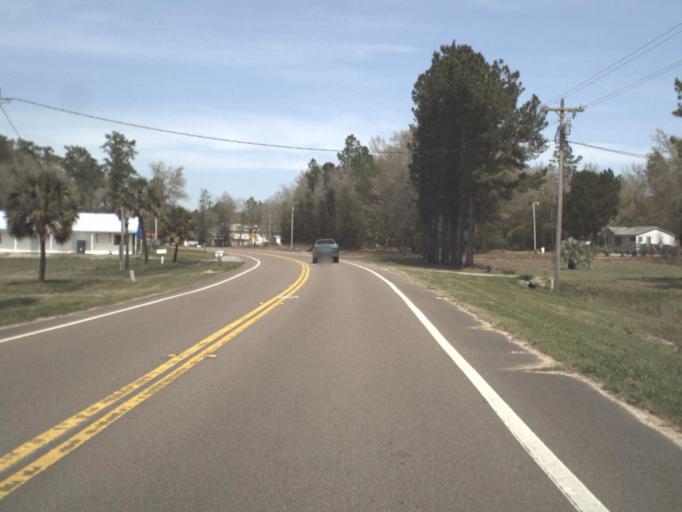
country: US
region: Florida
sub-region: Walton County
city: DeFuniak Springs
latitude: 30.7057
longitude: -85.9338
